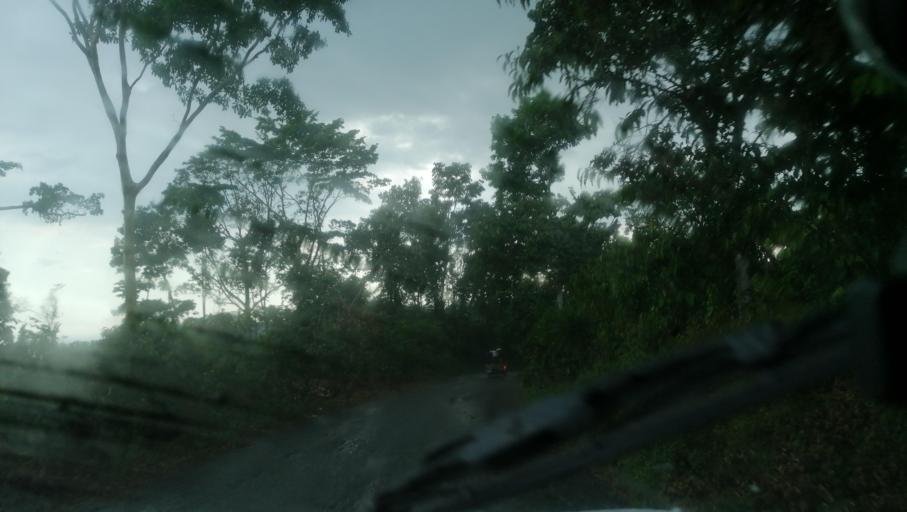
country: MX
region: Chiapas
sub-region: Cacahoatan
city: Benito Juarez
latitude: 15.0634
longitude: -92.1920
